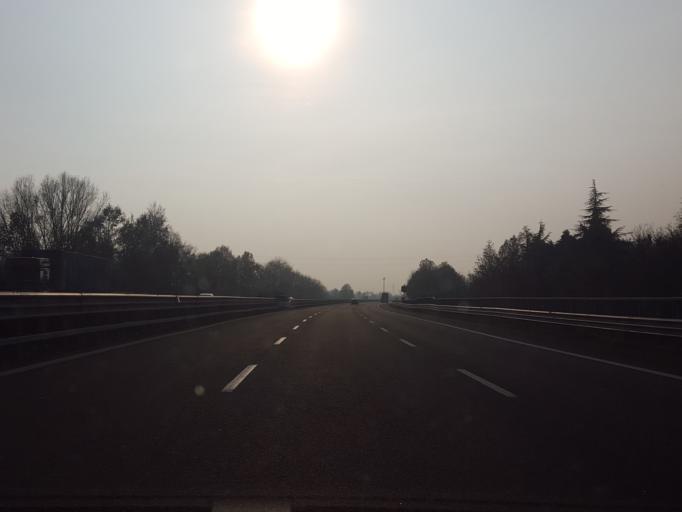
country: IT
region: Veneto
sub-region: Provincia di Treviso
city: Cendon
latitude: 45.6326
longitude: 12.3101
